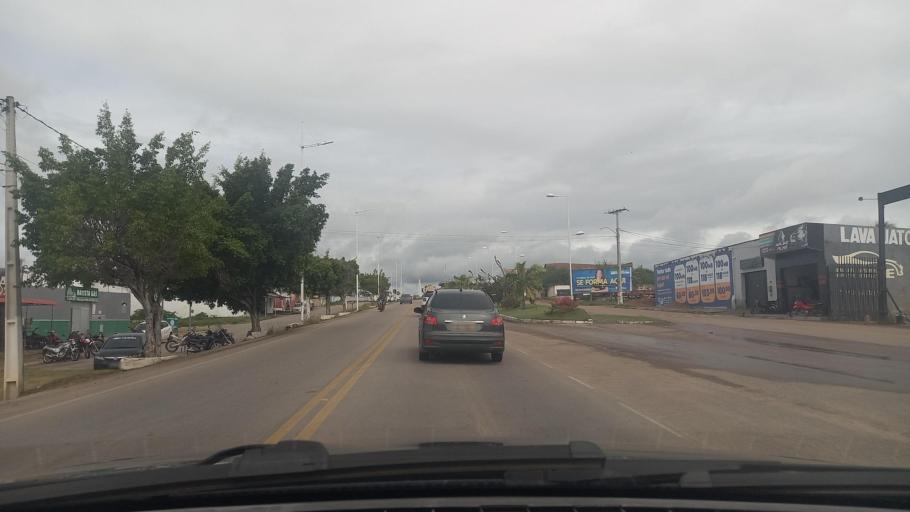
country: BR
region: Bahia
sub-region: Paulo Afonso
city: Paulo Afonso
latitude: -9.4440
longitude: -38.2227
